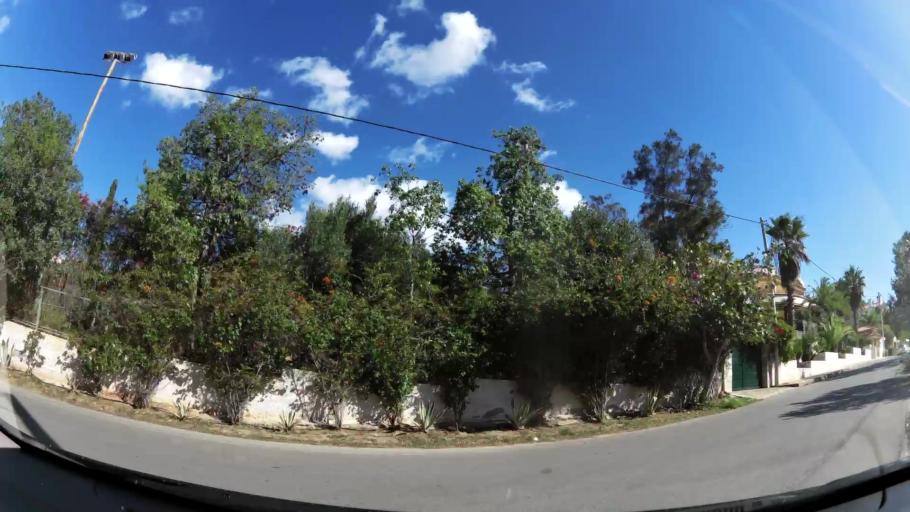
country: GR
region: Attica
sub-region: Nomarchia Anatolikis Attikis
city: Vouliagmeni
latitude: 37.8255
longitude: 23.7823
